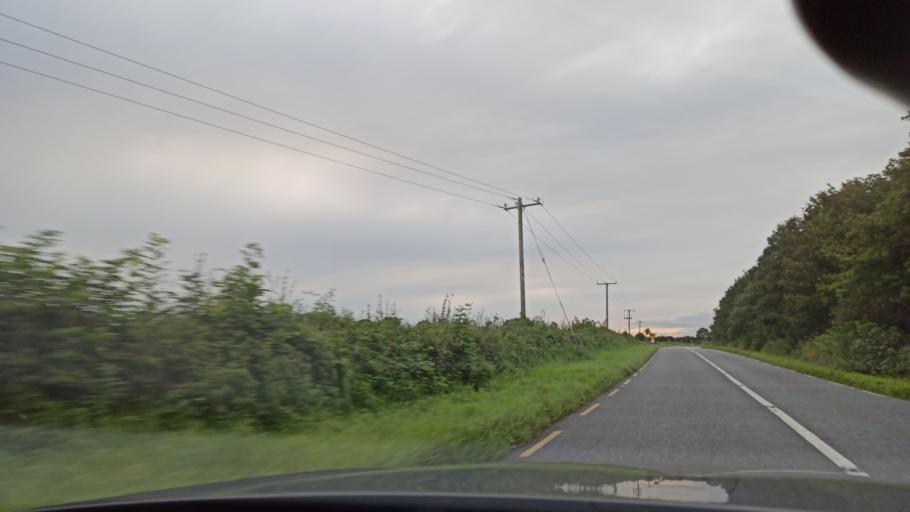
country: IE
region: Munster
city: Cashel
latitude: 52.4774
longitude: -7.8508
